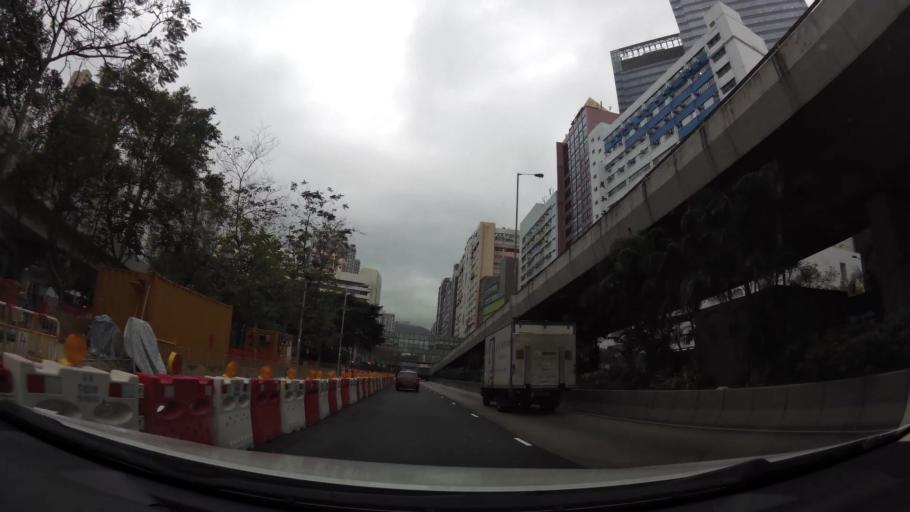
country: HK
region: Tsuen Wan
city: Tsuen Wan
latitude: 22.3612
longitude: 114.1314
